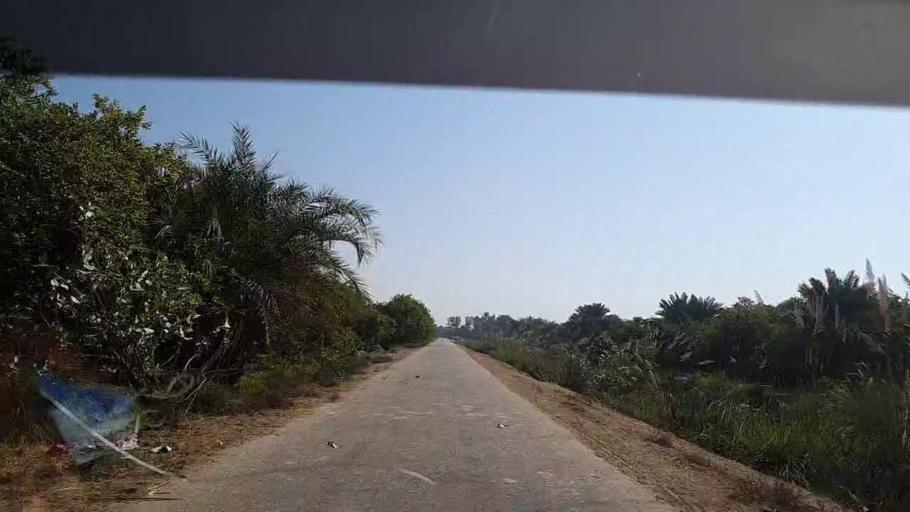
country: PK
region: Sindh
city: Larkana
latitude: 27.6032
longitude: 68.2641
